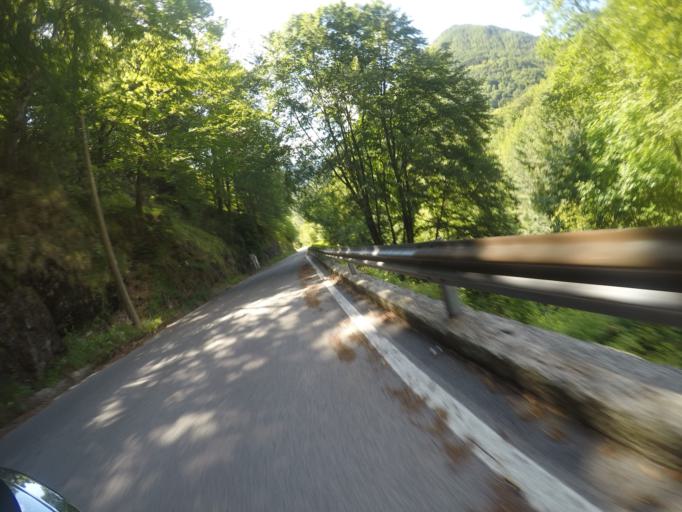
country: IT
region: Tuscany
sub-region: Provincia di Lucca
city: Fontana delle Monache
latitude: 44.0621
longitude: 10.2526
